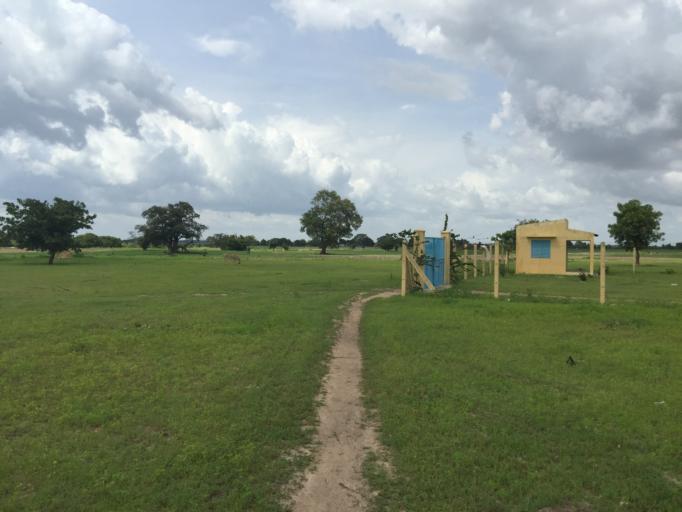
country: SN
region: Fatick
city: Sokone
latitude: 13.7554
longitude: -16.4262
